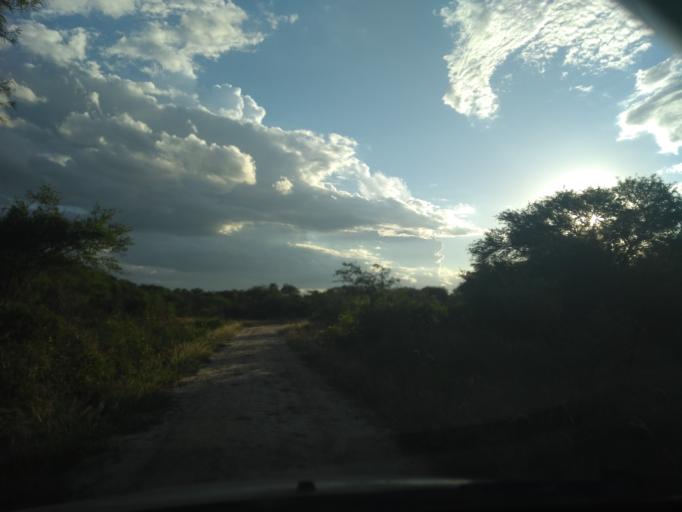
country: AR
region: Chaco
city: Colonia Benitez
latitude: -27.3904
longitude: -58.9429
